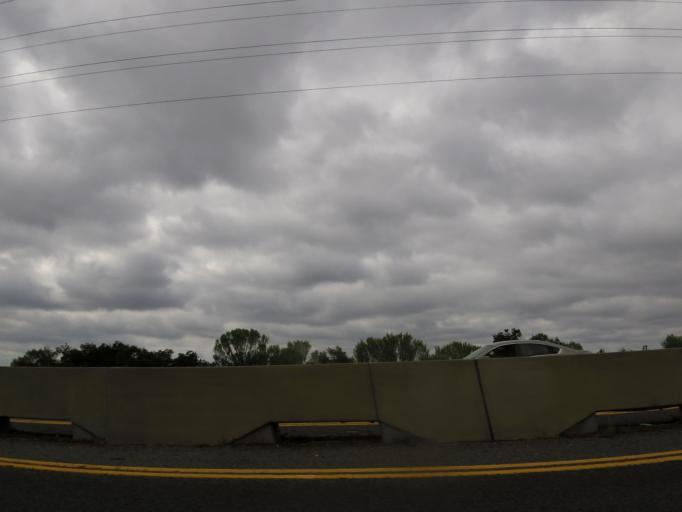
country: US
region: Georgia
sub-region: Glynn County
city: Saint Simon Mills
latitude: 31.1717
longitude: -81.4307
